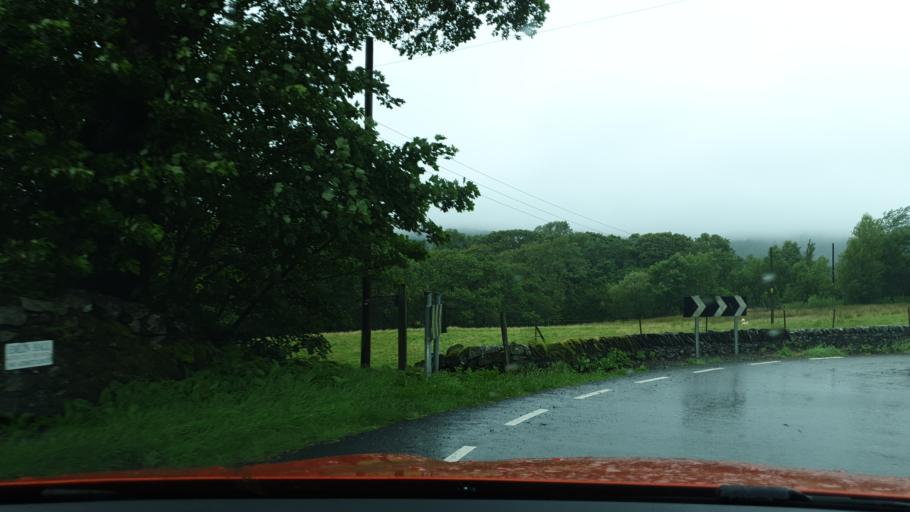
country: GB
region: England
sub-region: Cumbria
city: Ulverston
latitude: 54.3299
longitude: -3.0981
